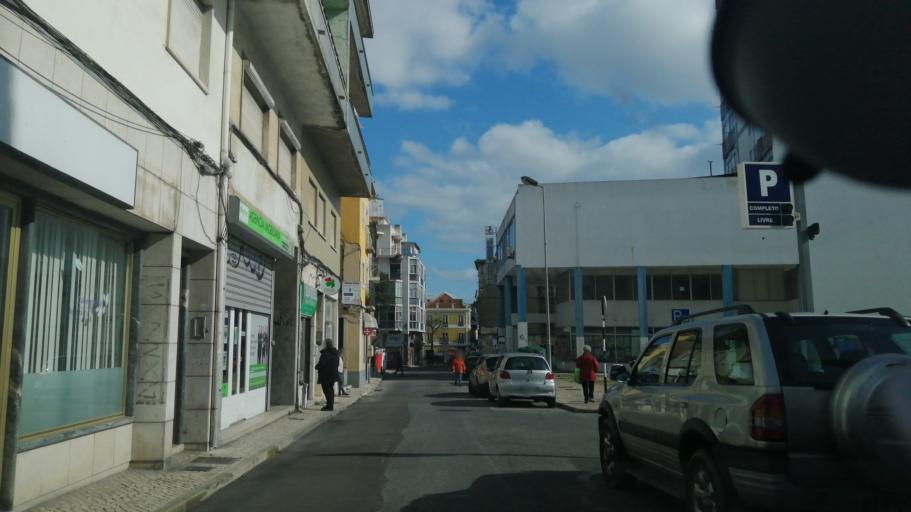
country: PT
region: Setubal
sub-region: Almada
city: Almada
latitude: 38.6812
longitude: -9.1599
